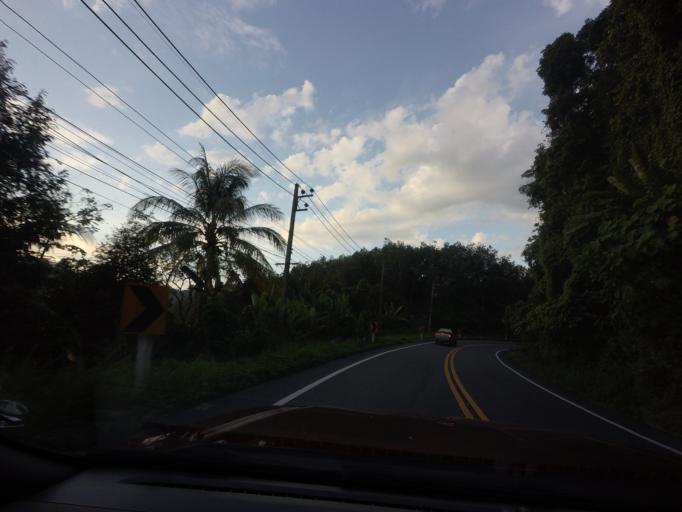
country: TH
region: Yala
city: Than To
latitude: 6.0387
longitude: 101.2058
